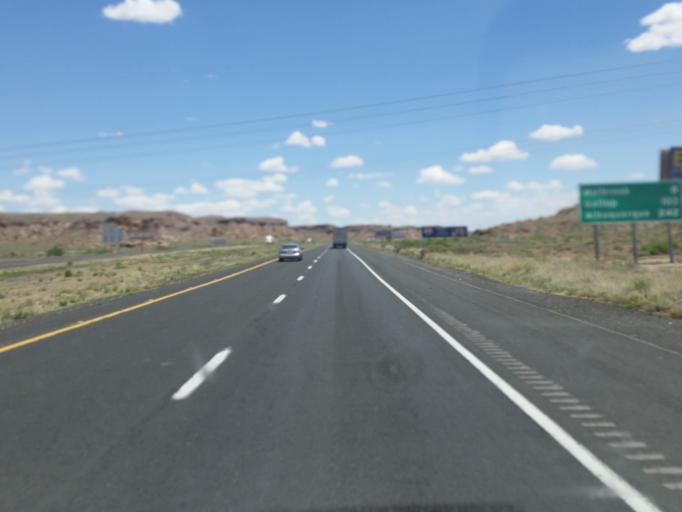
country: US
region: Arizona
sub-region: Navajo County
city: Joseph City
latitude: 34.9453
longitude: -110.2934
